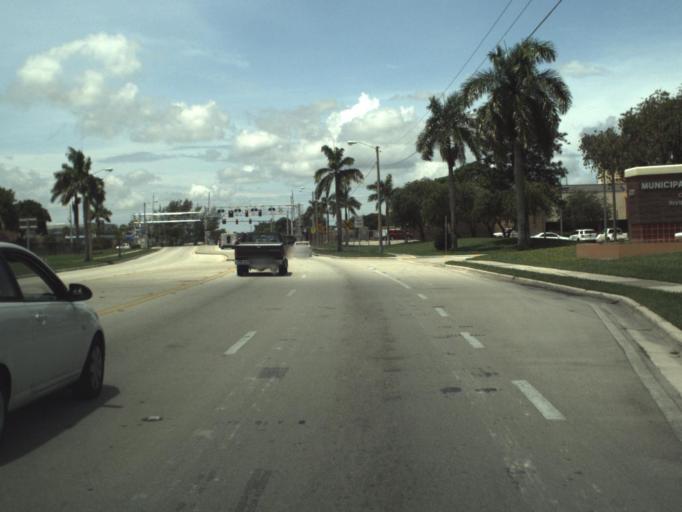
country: US
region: Florida
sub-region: Palm Beach County
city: Riviera Beach
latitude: 26.7834
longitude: -80.0648
